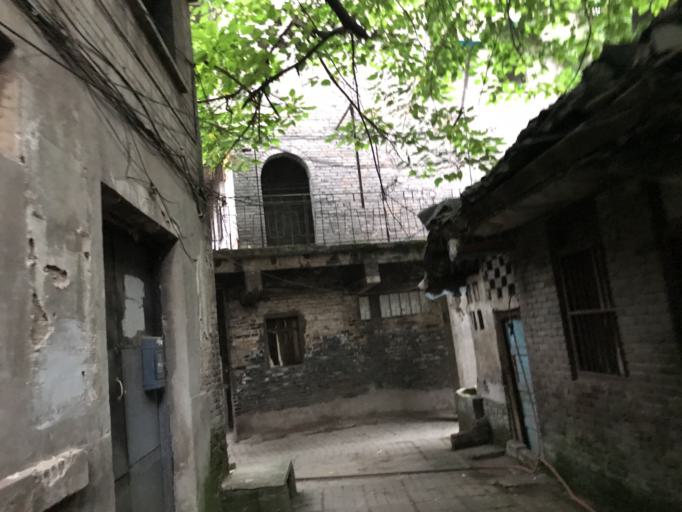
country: CN
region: Chongqing Shi
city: Nanping
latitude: 29.5607
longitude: 106.5930
